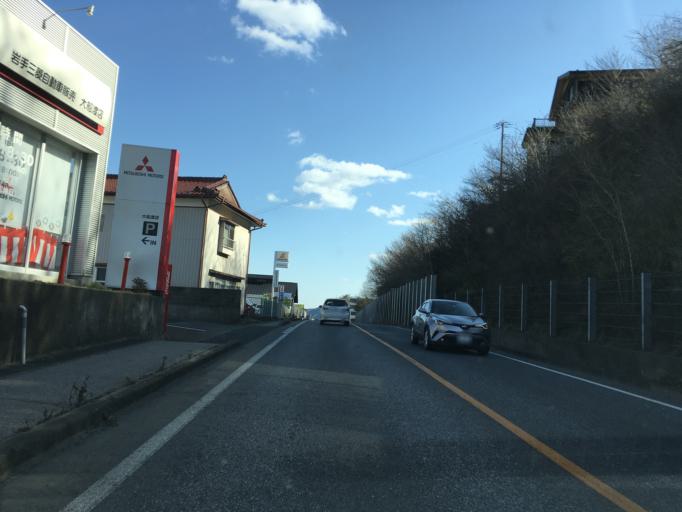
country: JP
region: Iwate
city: Ofunato
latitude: 39.0483
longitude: 141.7208
